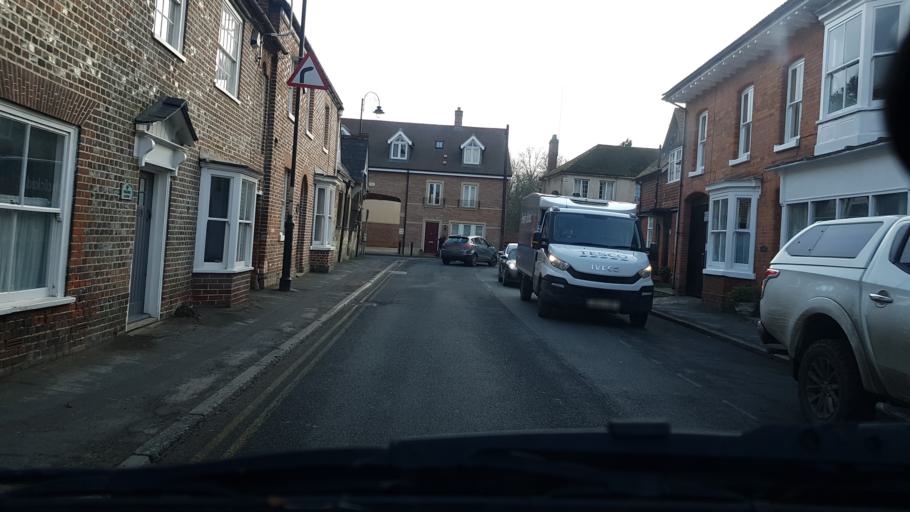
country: GB
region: England
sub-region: Wiltshire
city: Pewsey
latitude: 51.3387
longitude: -1.7650
